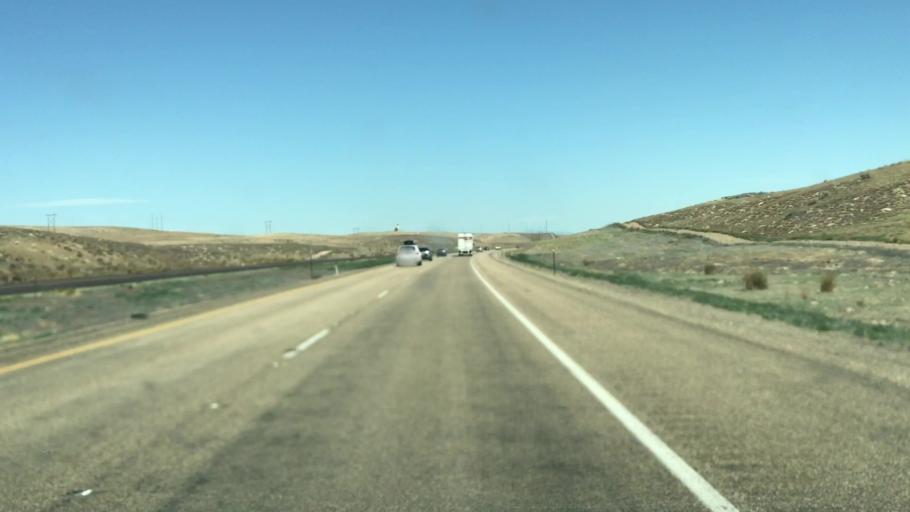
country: US
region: Idaho
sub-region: Payette County
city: New Plymouth
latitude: 43.8820
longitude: -116.7990
